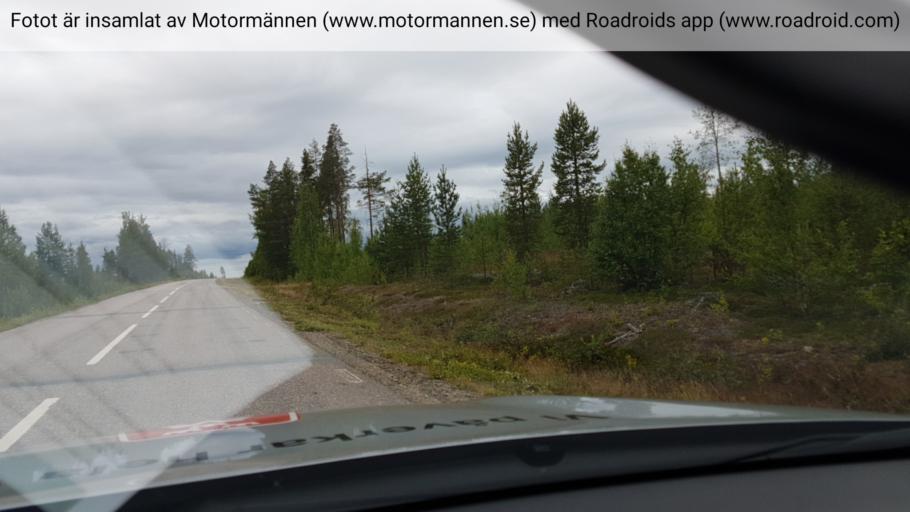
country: SE
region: Norrbotten
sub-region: Pajala Kommun
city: Pajala
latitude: 66.8245
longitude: 23.0243
